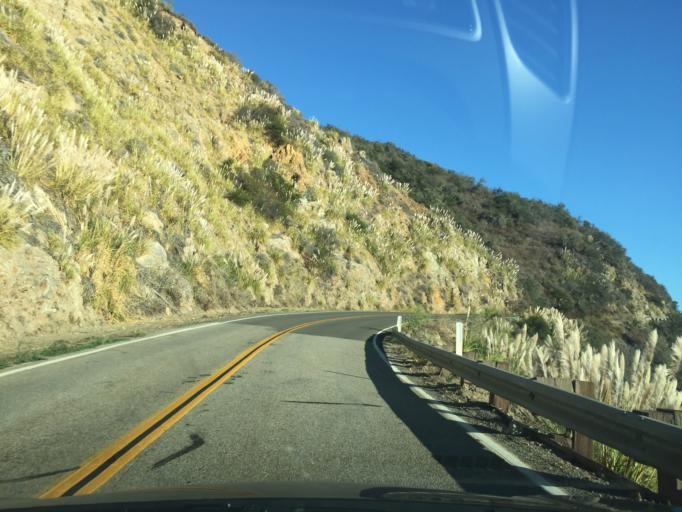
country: US
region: California
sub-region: San Luis Obispo County
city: Cambria
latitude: 35.8312
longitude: -121.3903
